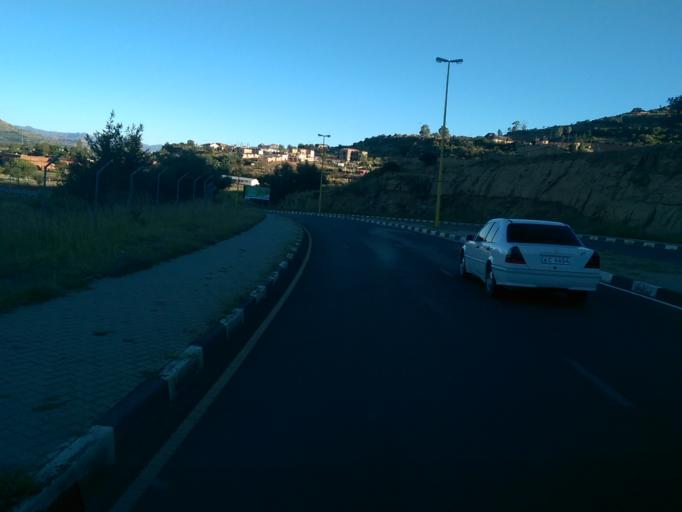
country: LS
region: Maseru
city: Maseru
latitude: -29.3246
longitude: 27.4968
